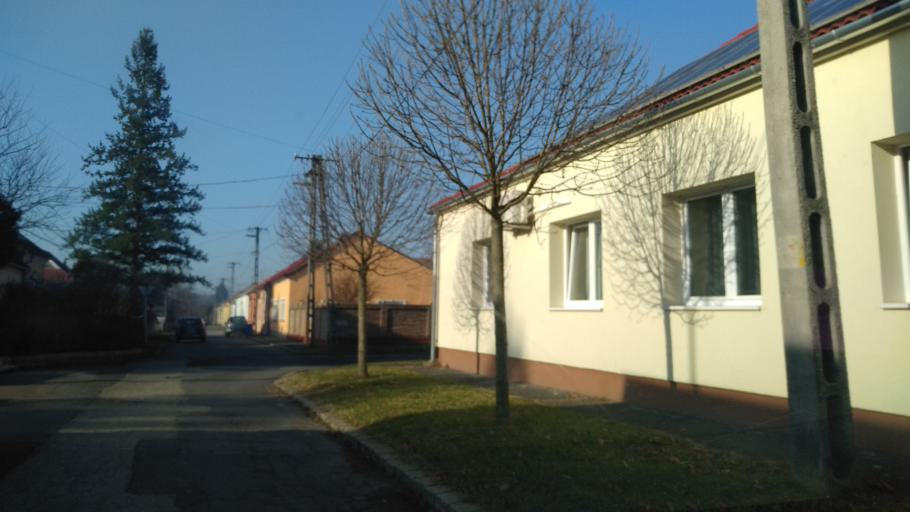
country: HU
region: Somogy
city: Barcs
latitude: 45.9581
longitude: 17.4593
